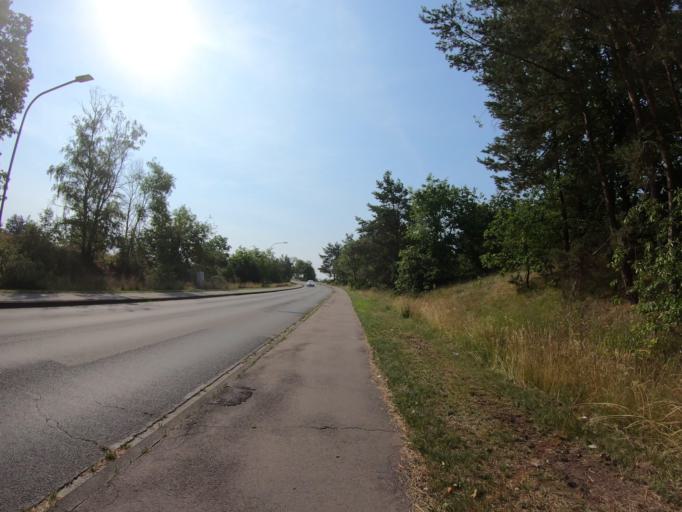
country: DE
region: Lower Saxony
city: Gifhorn
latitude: 52.4844
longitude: 10.5289
